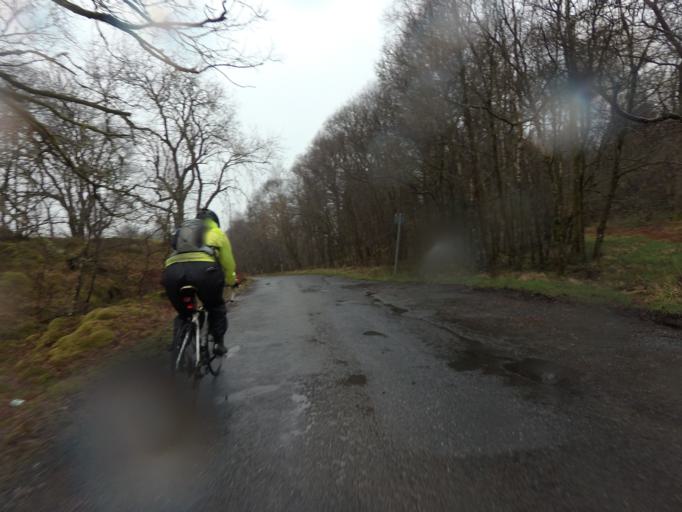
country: GB
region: Scotland
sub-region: West Dunbartonshire
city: Balloch
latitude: 56.2056
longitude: -4.5319
